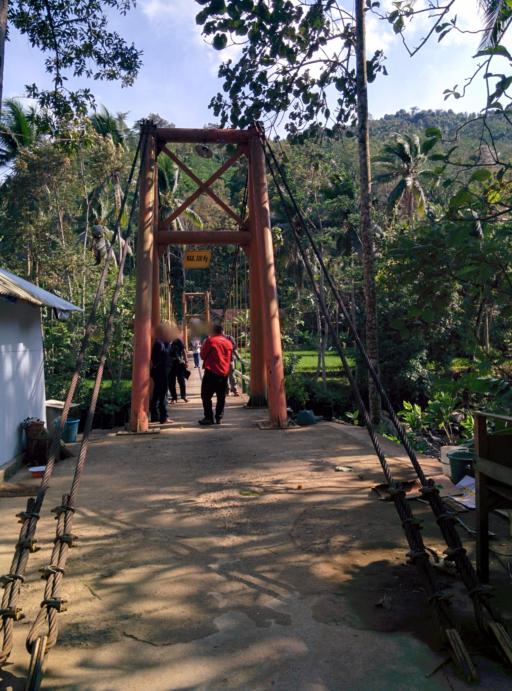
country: ID
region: East Java
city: Kedungbanteng Krajan
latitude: -8.3500
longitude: 112.7136
